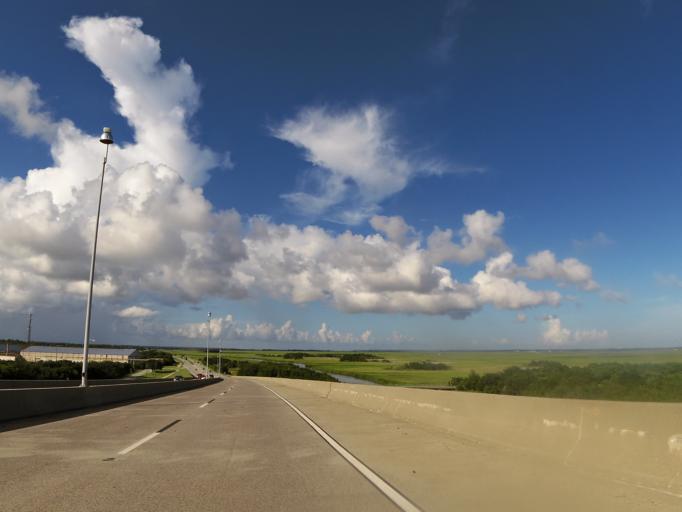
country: US
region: Georgia
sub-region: Glynn County
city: Brunswick
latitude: 31.1236
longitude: -81.4814
